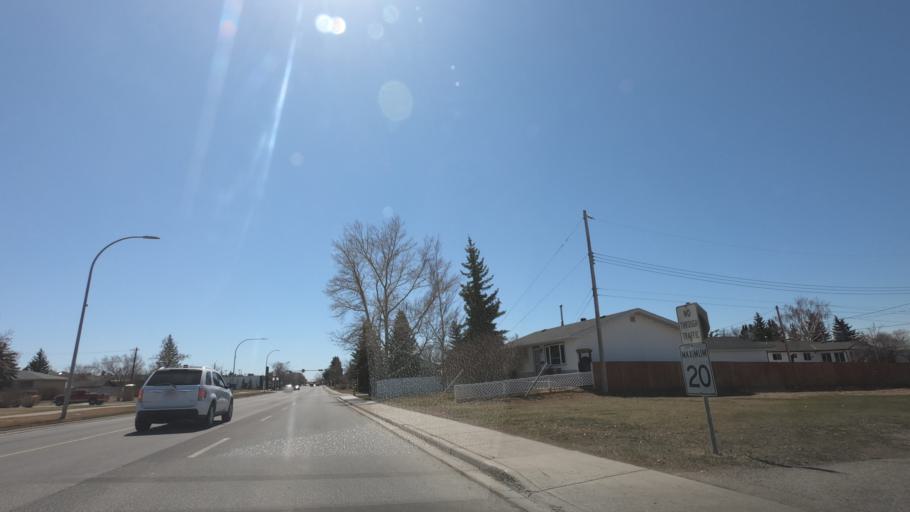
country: CA
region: Alberta
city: Airdrie
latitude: 51.2969
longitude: -114.0136
